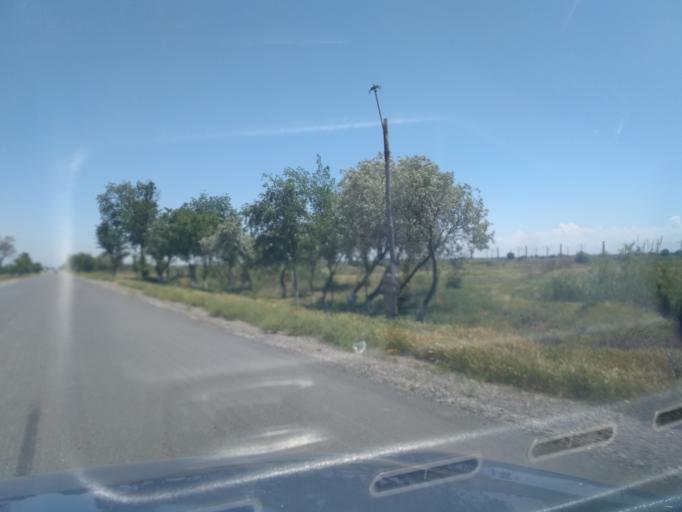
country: TJ
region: Viloyati Sughd
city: Zafarobod
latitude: 40.2138
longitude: 68.8660
